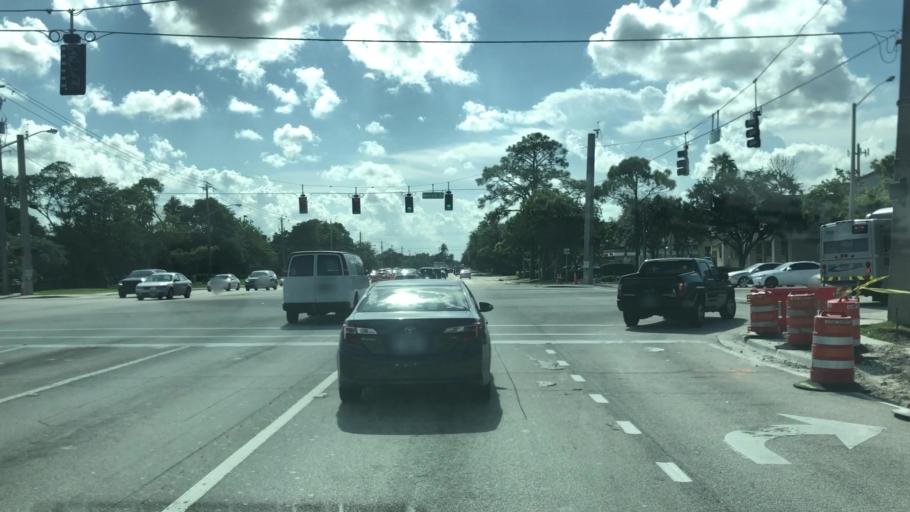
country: US
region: Florida
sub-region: Broward County
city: Parkland
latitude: 26.2868
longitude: -80.2339
